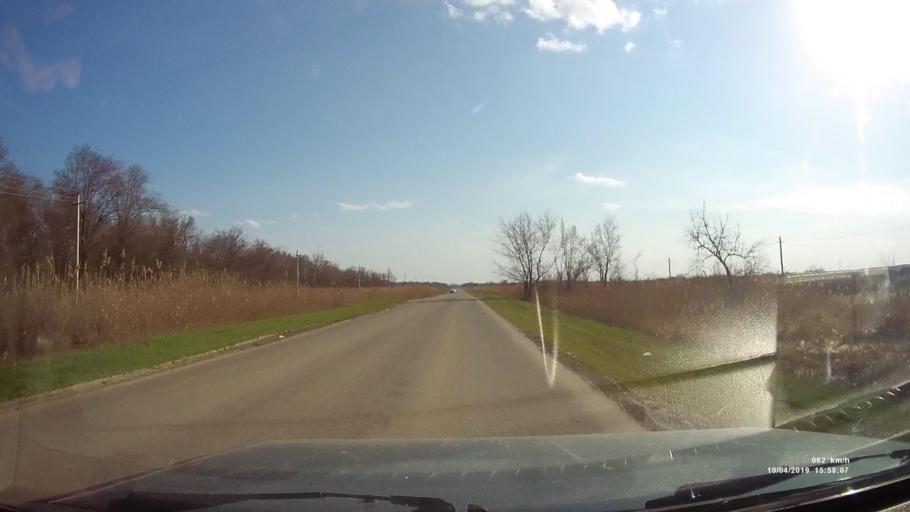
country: RU
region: Rostov
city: Masalovka
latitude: 48.4056
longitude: 40.2734
